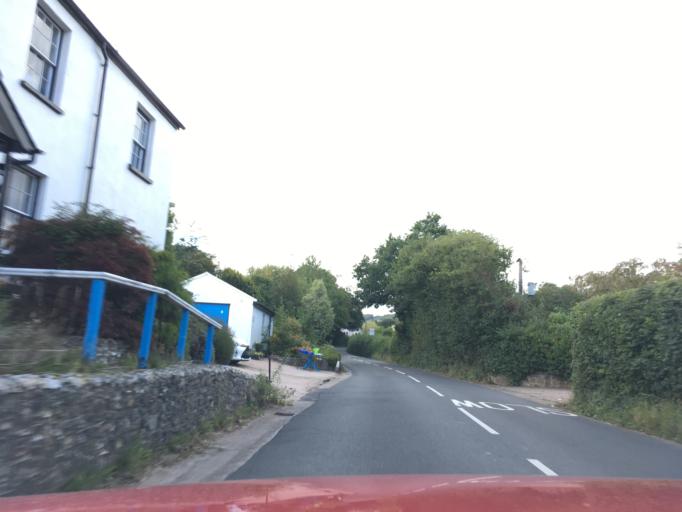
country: GB
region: England
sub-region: Devon
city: Sidmouth
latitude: 50.7218
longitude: -3.2190
